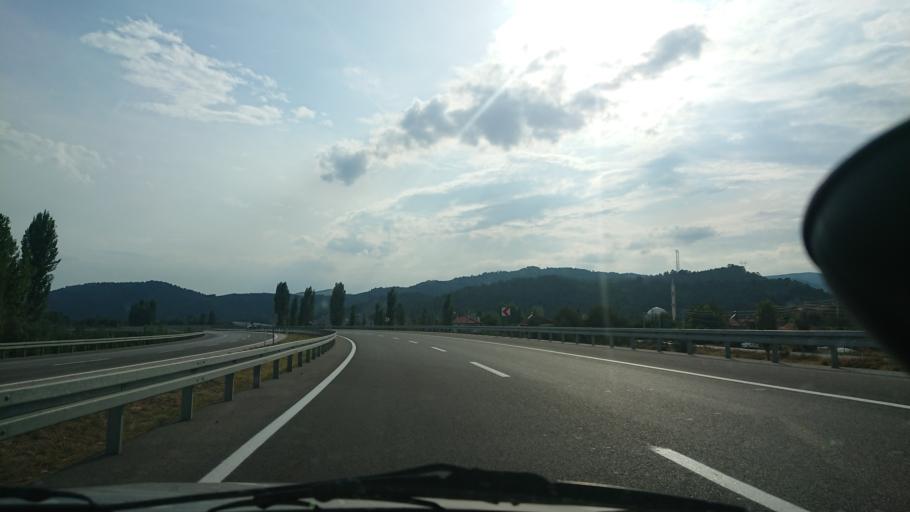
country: TR
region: Kuetahya
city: Gediz
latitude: 38.9315
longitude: 29.3067
